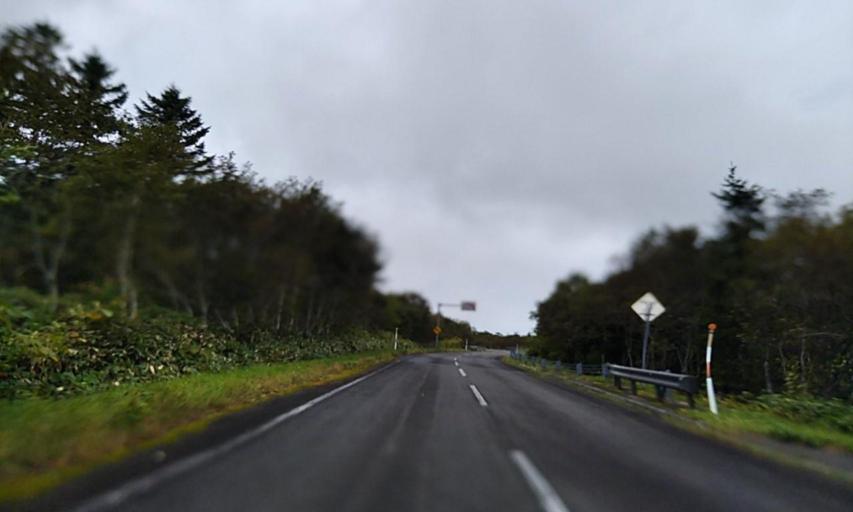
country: JP
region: Hokkaido
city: Abashiri
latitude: 43.6025
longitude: 144.5763
